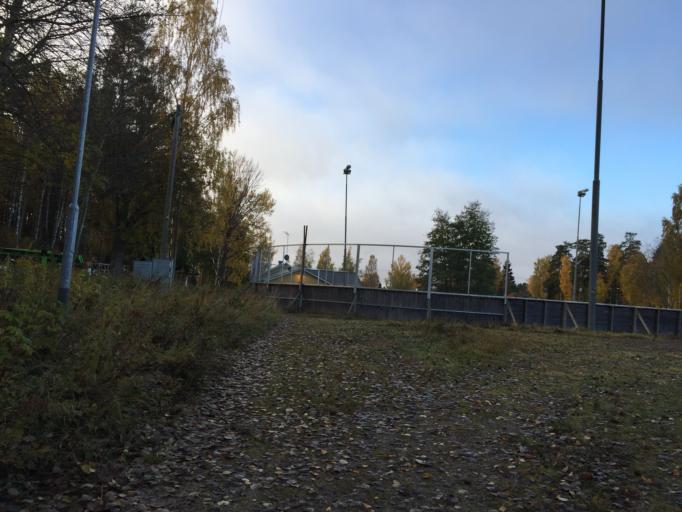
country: SE
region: Vaestmanland
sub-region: Hallstahammars Kommun
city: Hallstahammar
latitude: 59.6261
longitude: 16.2467
